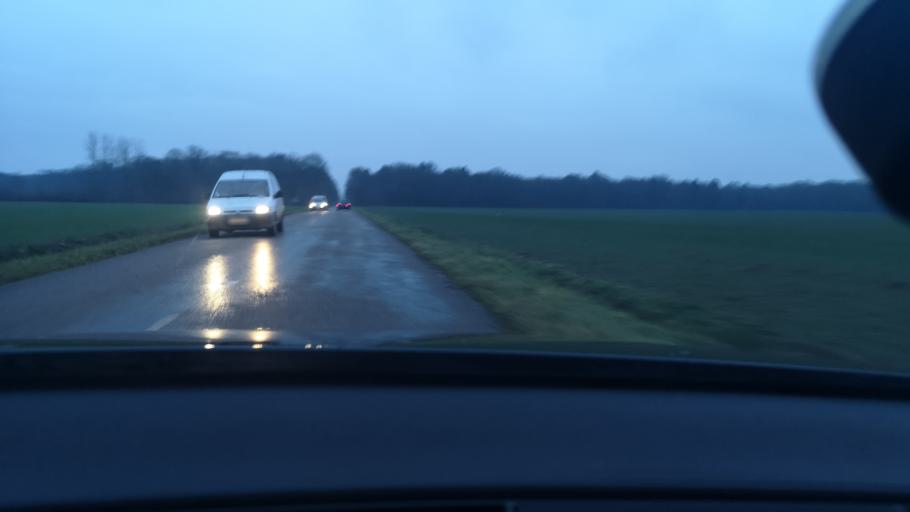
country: FR
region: Bourgogne
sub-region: Departement de la Cote-d'Or
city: Seurre
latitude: 47.0254
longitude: 5.0602
